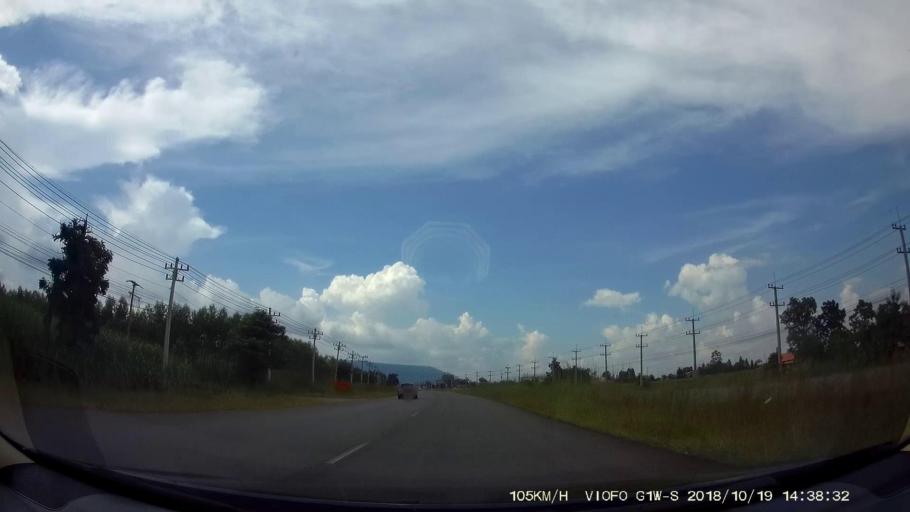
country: TH
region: Chaiyaphum
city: Kaeng Khro
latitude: 16.2146
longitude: 102.2011
